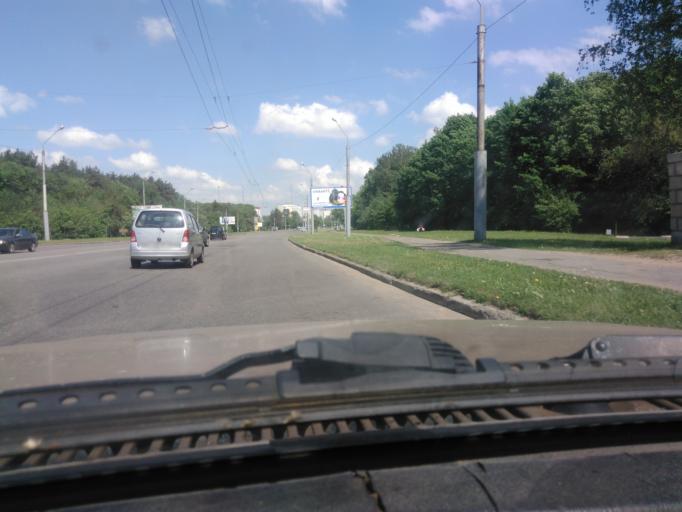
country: BY
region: Mogilev
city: Mahilyow
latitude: 53.9438
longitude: 30.3552
